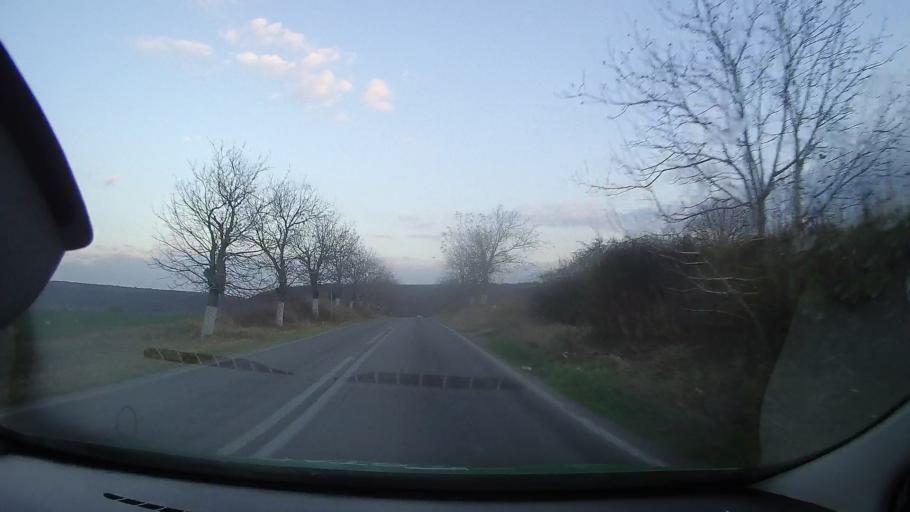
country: RO
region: Constanta
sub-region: Comuna Lipnita
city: Lipnita
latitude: 44.0957
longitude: 27.6370
